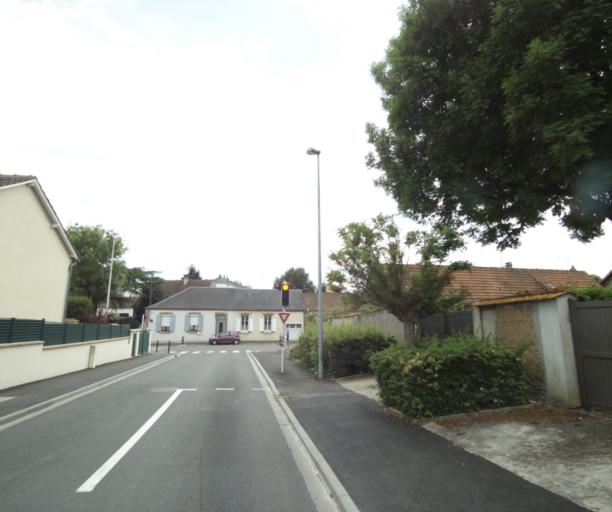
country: FR
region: Centre
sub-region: Departement d'Eure-et-Loir
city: Luce
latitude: 48.4392
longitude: 1.4582
